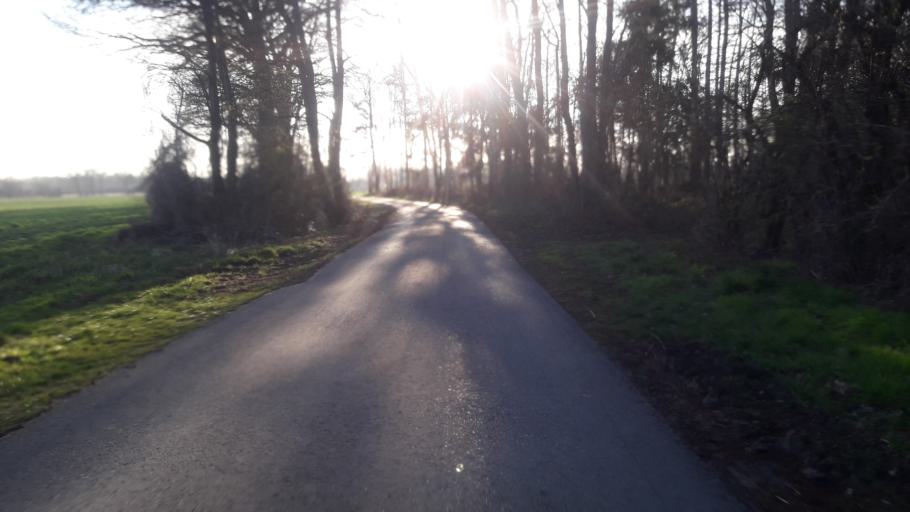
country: DE
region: North Rhine-Westphalia
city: Rietberg
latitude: 51.7882
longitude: 8.4640
